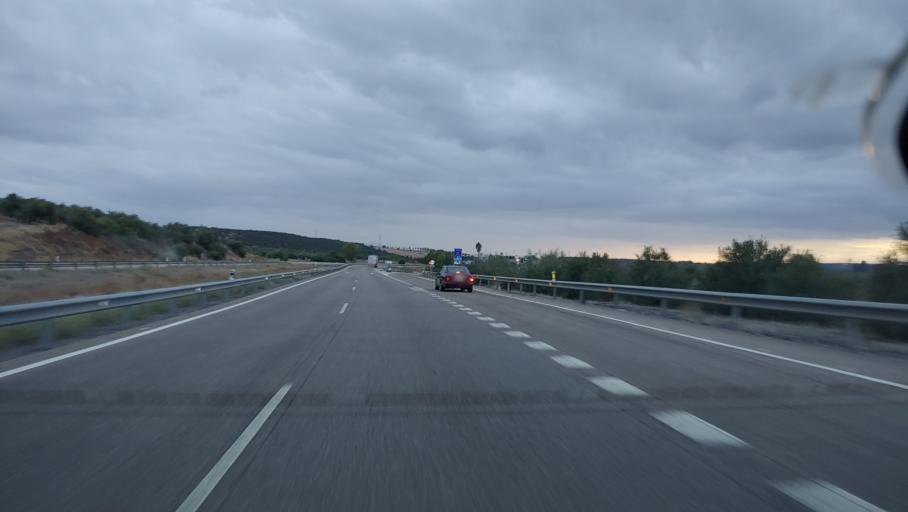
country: ES
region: Andalusia
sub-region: Provincia de Jaen
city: Guarroman
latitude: 38.1701
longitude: -3.7074
